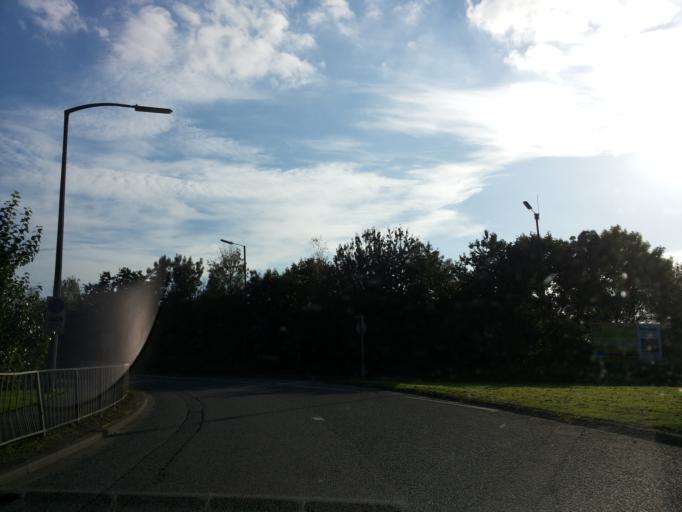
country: GB
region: England
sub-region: Doncaster
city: Hatfield
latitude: 53.6181
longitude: -0.9764
